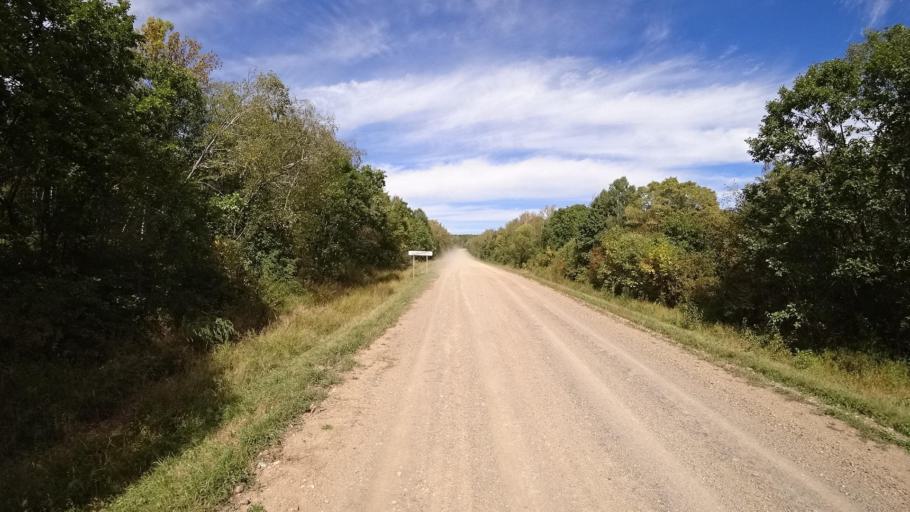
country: RU
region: Primorskiy
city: Yakovlevka
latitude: 44.6537
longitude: 133.5971
